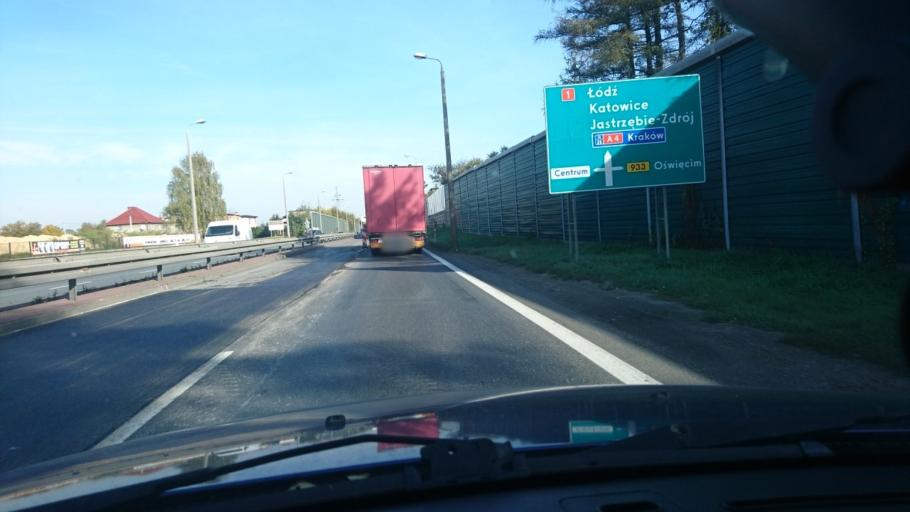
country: PL
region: Silesian Voivodeship
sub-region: Powiat pszczynski
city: Pszczyna
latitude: 49.9710
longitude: 18.9584
